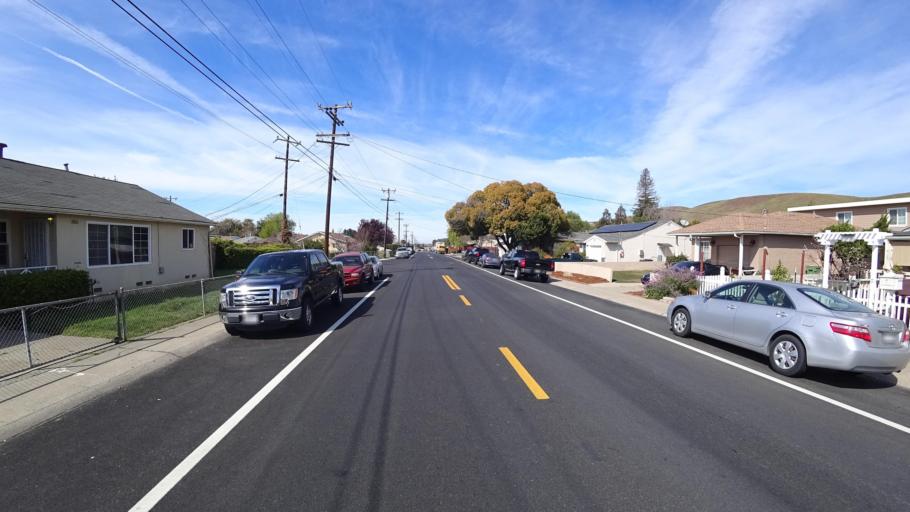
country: US
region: California
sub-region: Alameda County
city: Union City
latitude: 37.6091
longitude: -122.0250
